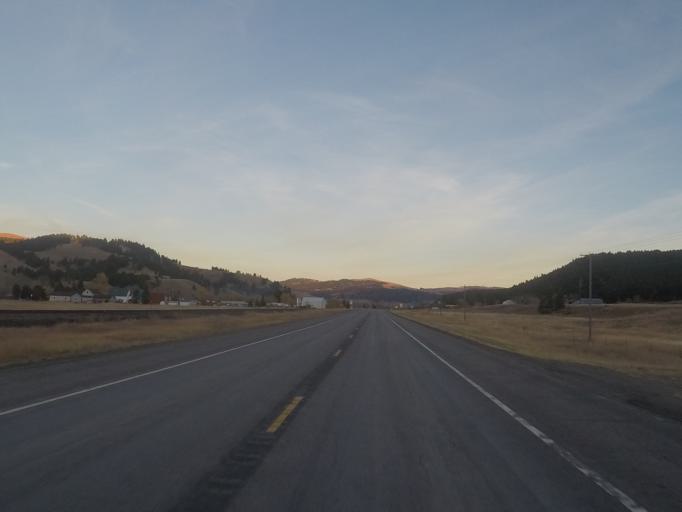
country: US
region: Montana
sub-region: Lewis and Clark County
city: Helena West Side
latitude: 46.5635
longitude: -112.4402
